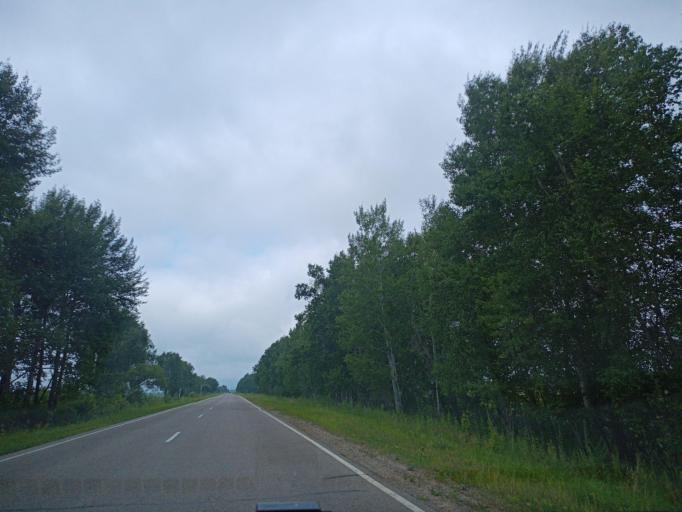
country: RU
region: Primorskiy
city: Novopokrovka
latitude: 45.9783
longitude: 134.1763
